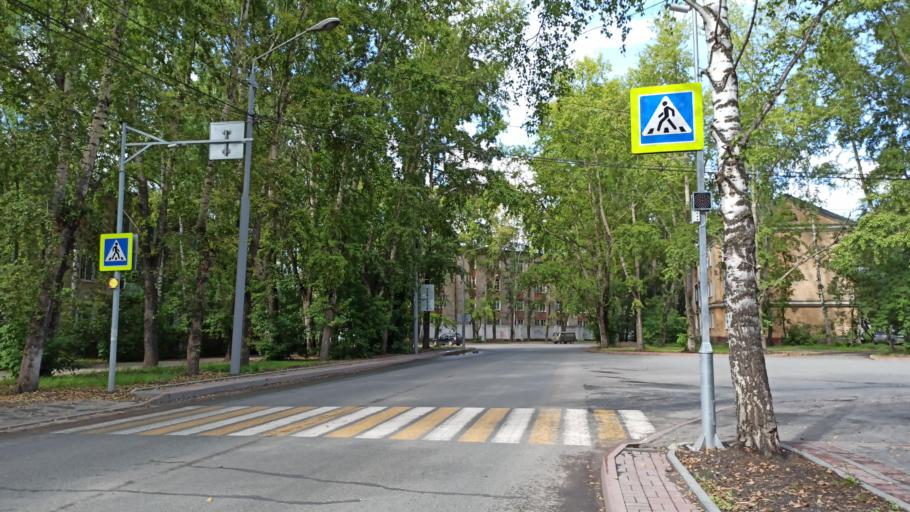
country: RU
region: Tomsk
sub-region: Tomskiy Rayon
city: Tomsk
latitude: 56.4627
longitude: 84.9814
